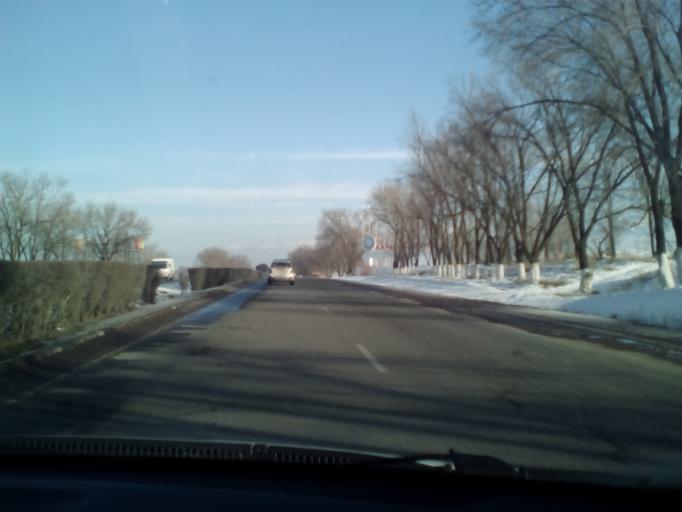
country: KZ
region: Almaty Oblysy
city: Burunday
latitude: 43.2210
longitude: 76.4493
